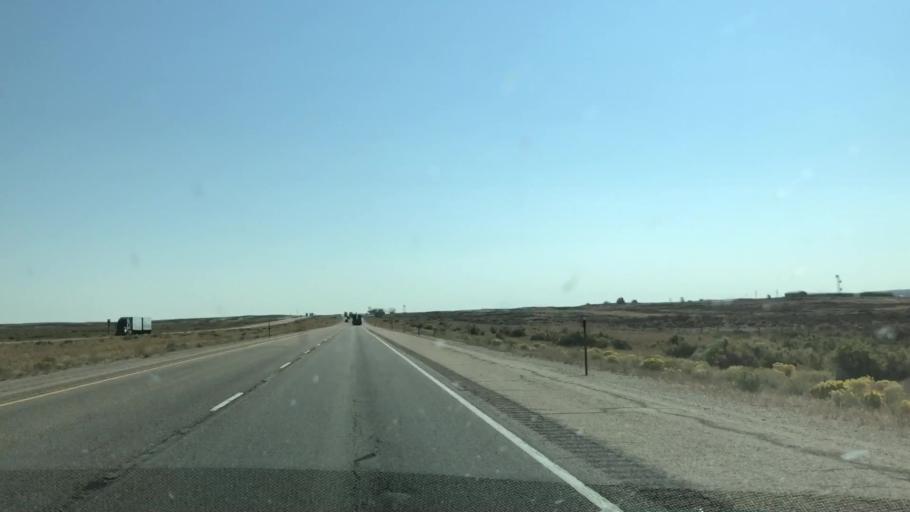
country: US
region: Wyoming
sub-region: Sweetwater County
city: Rock Springs
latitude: 41.6358
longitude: -108.4232
